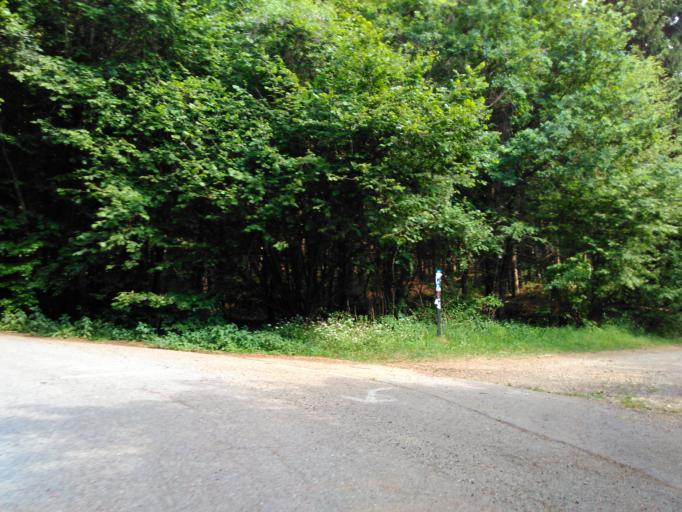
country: LU
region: Luxembourg
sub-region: Canton d'Esch-sur-Alzette
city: Esch-sur-Alzette
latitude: 49.4715
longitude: 5.9953
